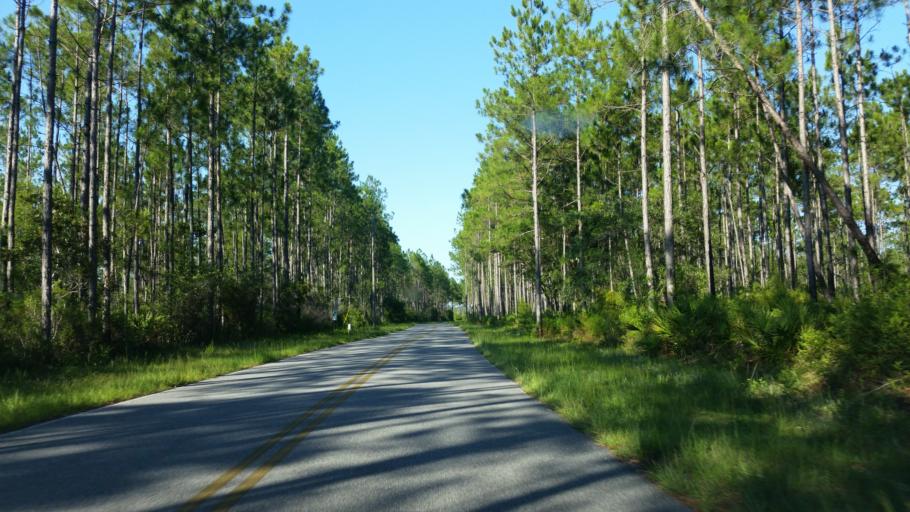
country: US
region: Florida
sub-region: Escambia County
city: Bellview
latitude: 30.4707
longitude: -87.4028
